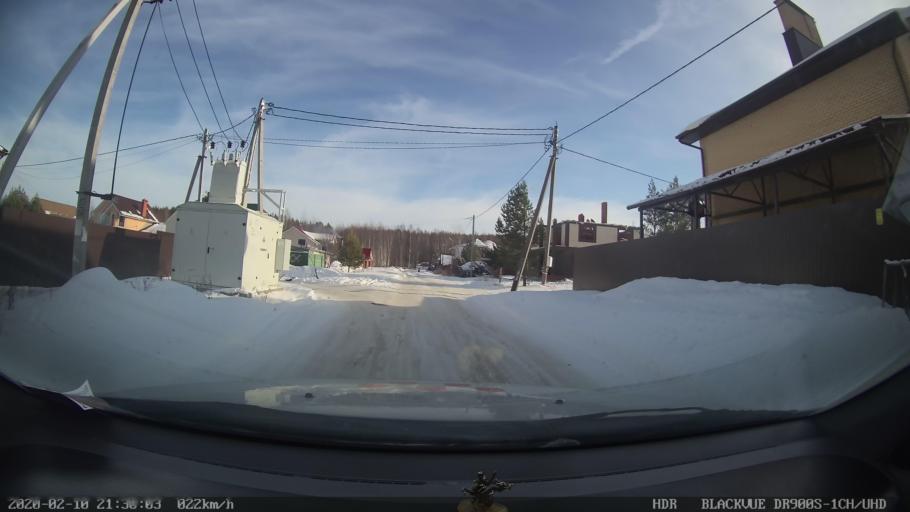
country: RU
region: Tatarstan
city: Vysokaya Gora
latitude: 55.7796
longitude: 49.2751
